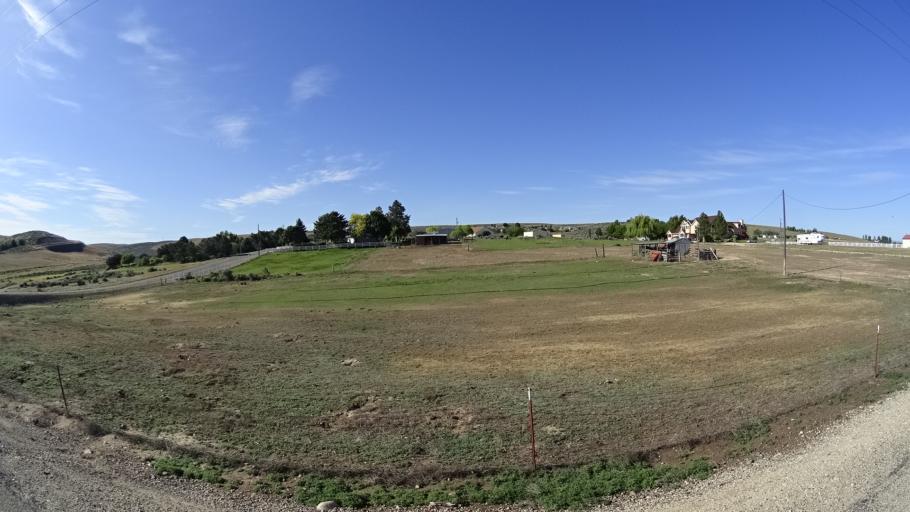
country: US
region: Idaho
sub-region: Ada County
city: Garden City
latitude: 43.5247
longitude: -116.2815
